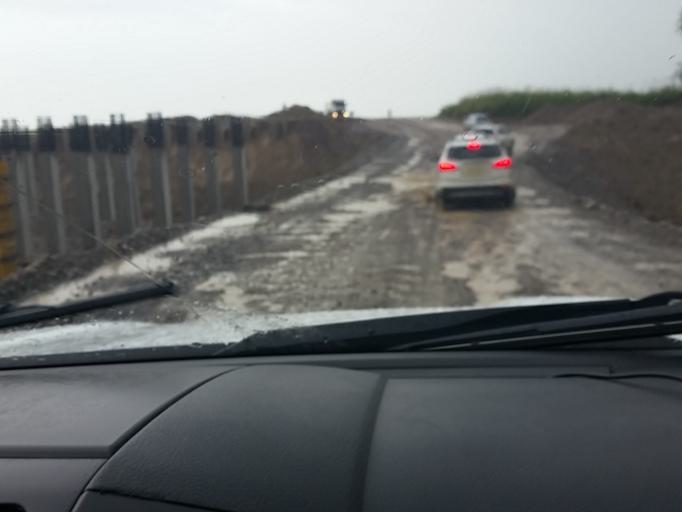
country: KZ
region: Almaty Oblysy
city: Turgen'
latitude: 43.5217
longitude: 77.5268
